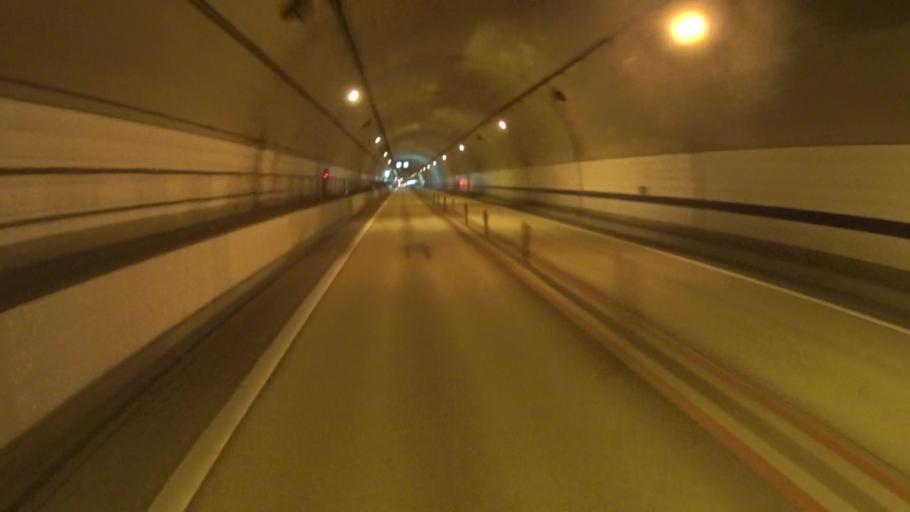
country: JP
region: Kyoto
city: Miyazu
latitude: 35.4873
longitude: 135.1723
